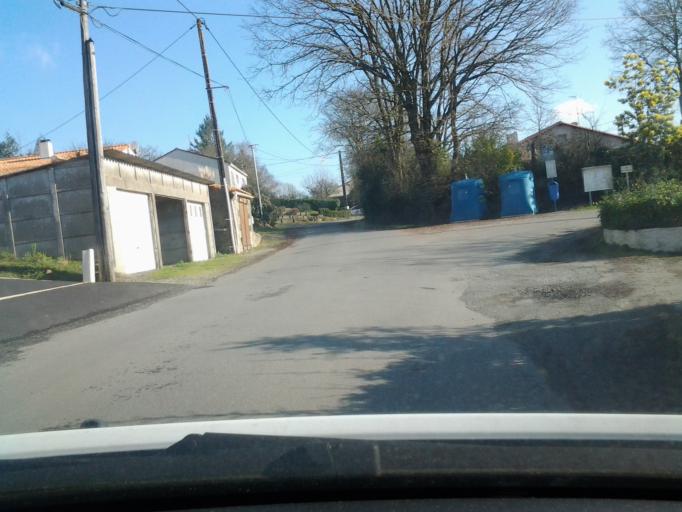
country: FR
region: Pays de la Loire
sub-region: Departement de la Vendee
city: Dompierre-sur-Yon
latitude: 46.7208
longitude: -1.4023
